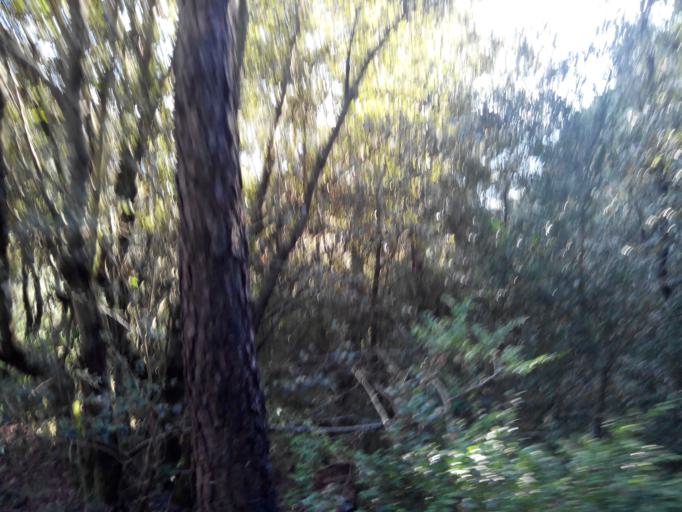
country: ES
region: Catalonia
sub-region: Provincia de Barcelona
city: Vilada
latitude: 42.1136
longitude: 1.9355
